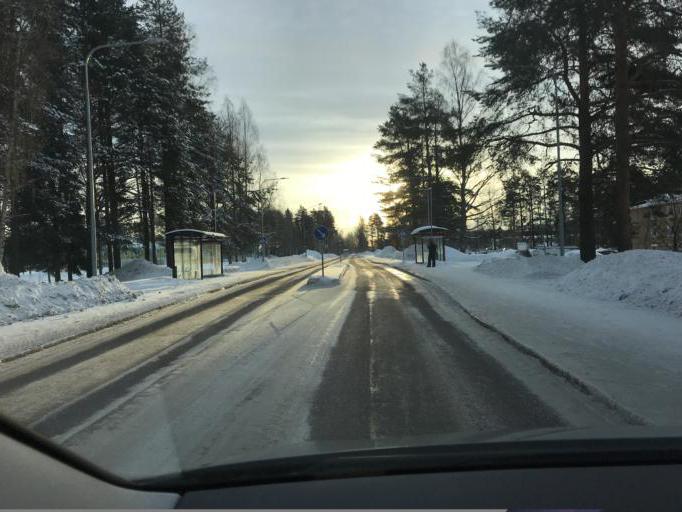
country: SE
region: Norrbotten
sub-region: Lulea Kommun
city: Bergnaset
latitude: 65.6072
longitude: 22.1078
